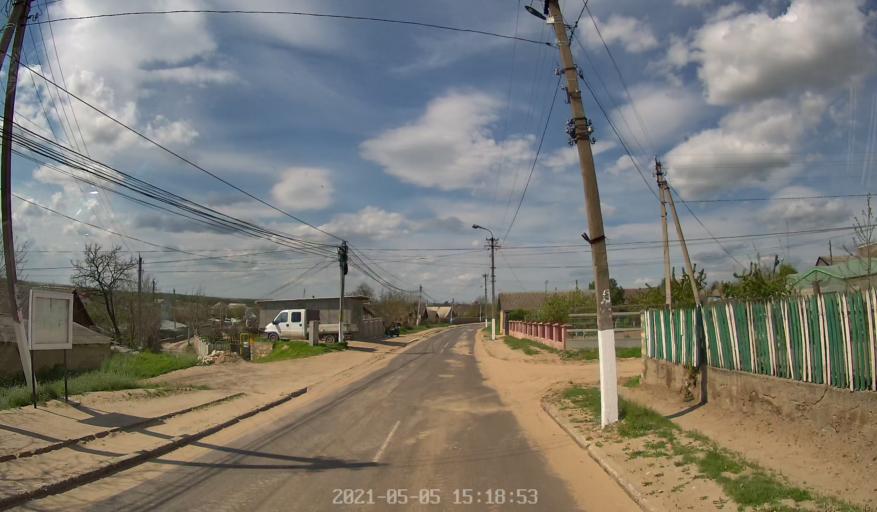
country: MD
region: Criuleni
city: Criuleni
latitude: 47.1231
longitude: 29.1940
